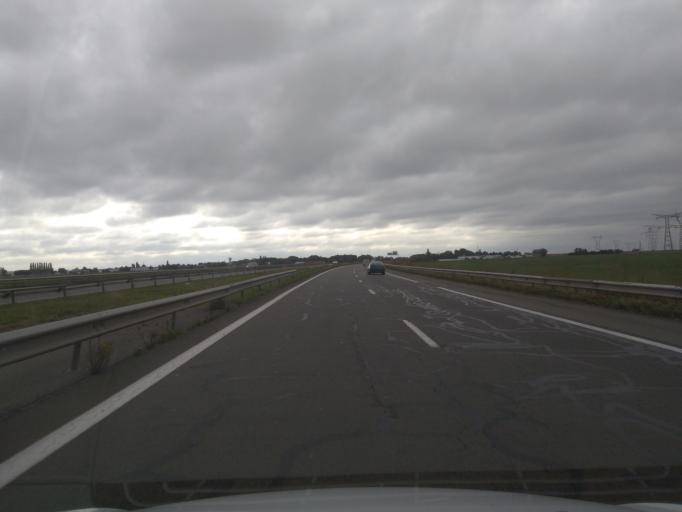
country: FR
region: Nord-Pas-de-Calais
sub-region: Departement du Nord
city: Orchies
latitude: 50.4854
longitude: 3.2163
